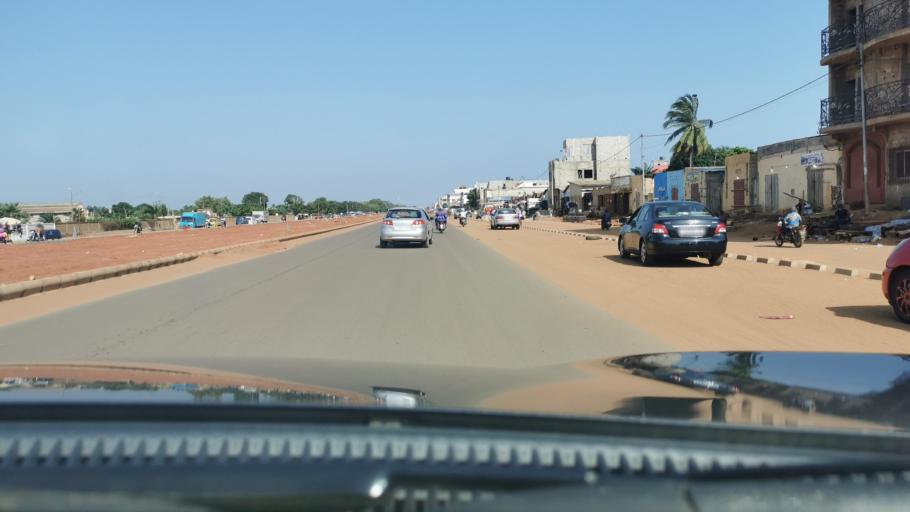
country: TG
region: Maritime
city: Lome
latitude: 6.2003
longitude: 1.1489
